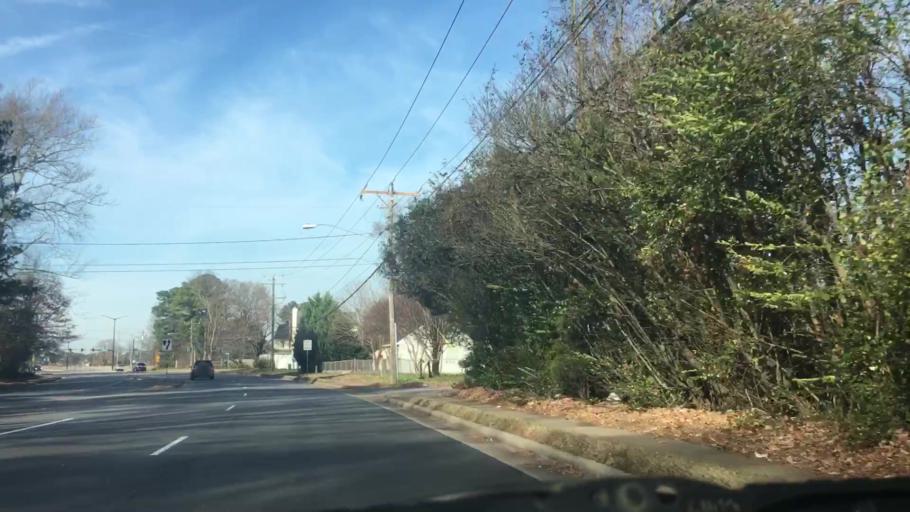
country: US
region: Virginia
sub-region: City of Chesapeake
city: Chesapeake
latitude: 36.8246
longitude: -76.1543
